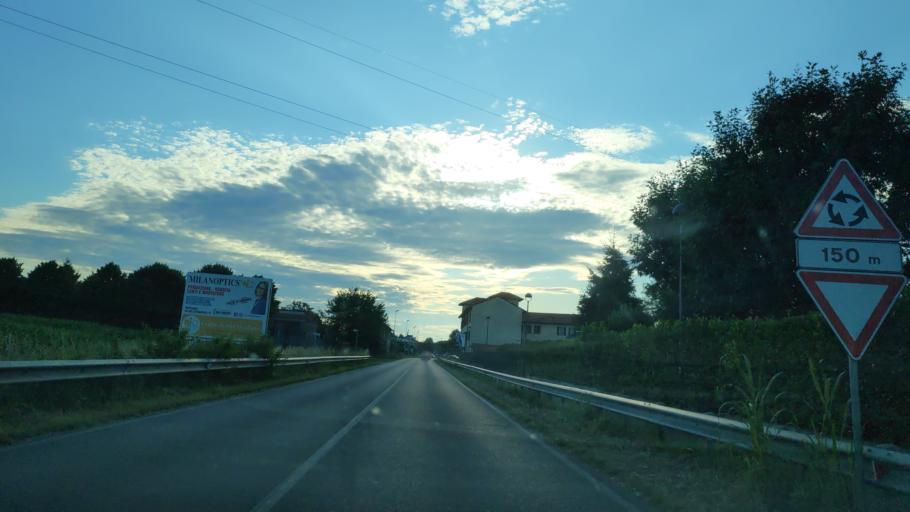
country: IT
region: Lombardy
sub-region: Citta metropolitana di Milano
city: Vigliano-Bettolino
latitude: 45.4322
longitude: 9.3440
